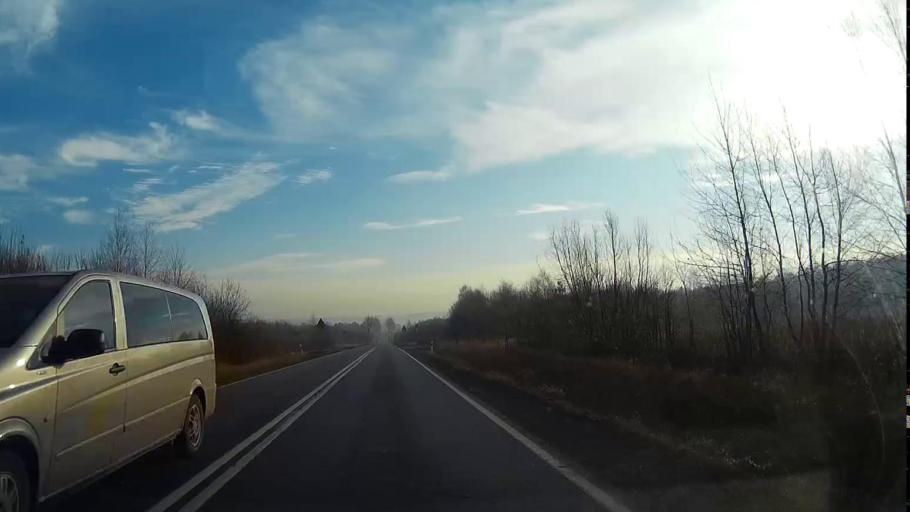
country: PL
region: Lesser Poland Voivodeship
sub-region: Powiat chrzanowski
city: Kwaczala
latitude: 50.0607
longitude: 19.5082
